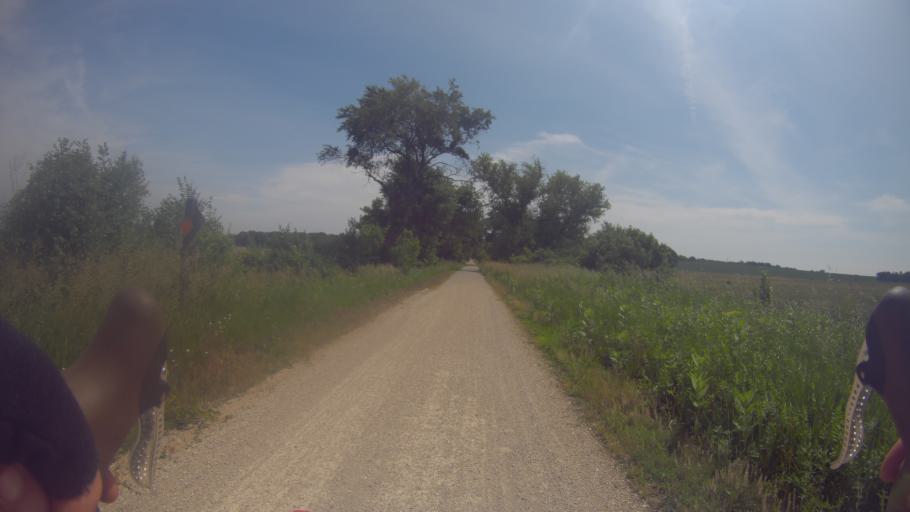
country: US
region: Wisconsin
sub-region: Jefferson County
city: Lake Ripley
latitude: 43.0618
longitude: -88.9679
